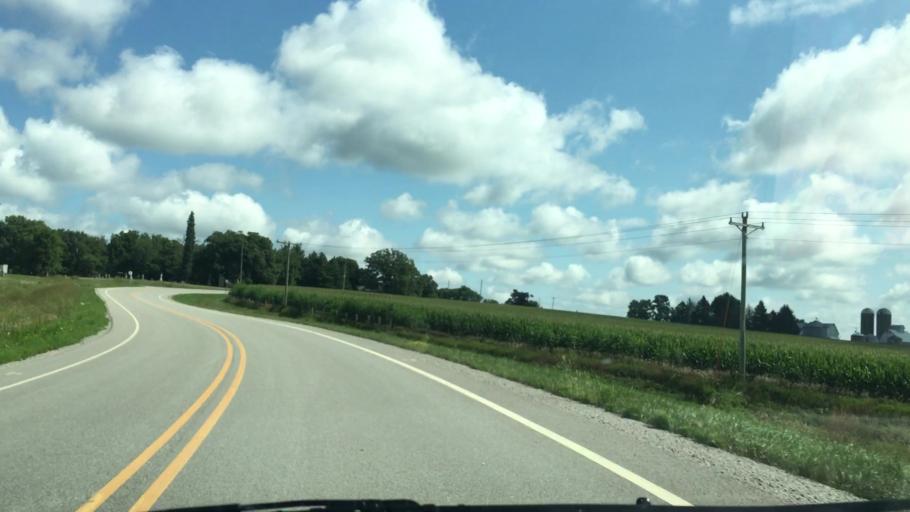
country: US
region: Iowa
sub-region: Johnson County
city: Solon
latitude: 41.8395
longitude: -91.4250
